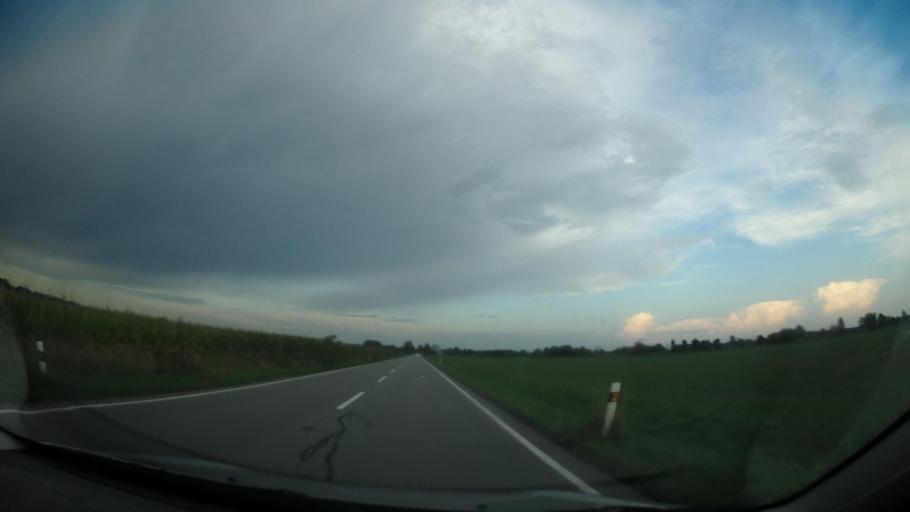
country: CZ
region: Olomoucky
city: Troubky
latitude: 49.4260
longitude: 17.3198
